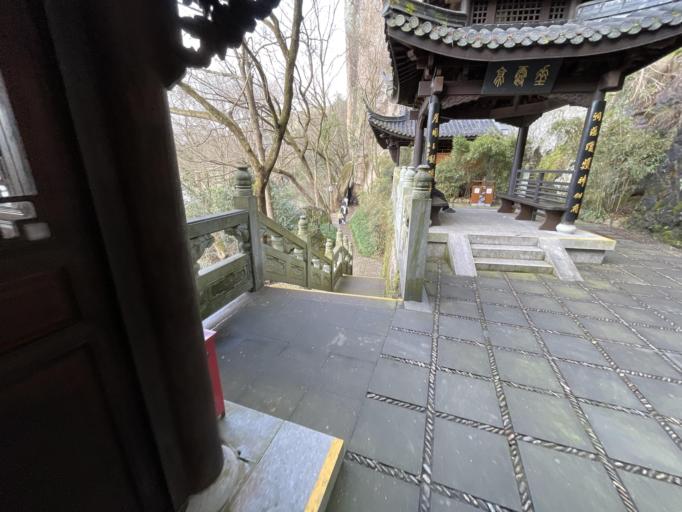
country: CN
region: Zhejiang Sheng
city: Shuhong
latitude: 28.6932
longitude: 120.1394
